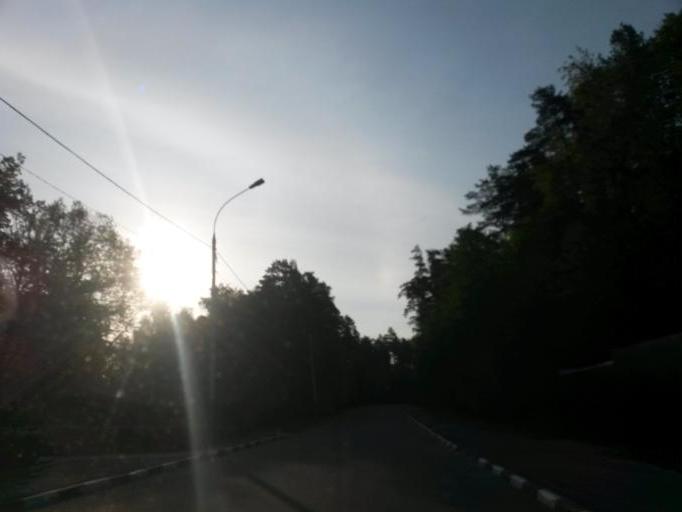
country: RU
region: Moskovskaya
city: Shcherbinka
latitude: 55.5047
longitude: 37.6182
